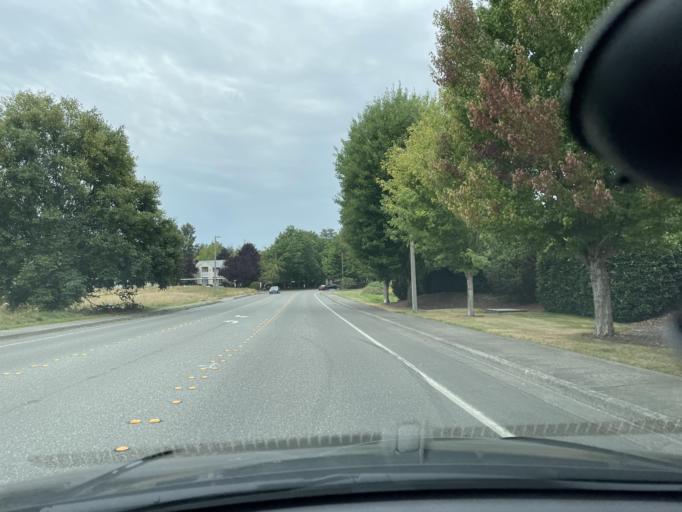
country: US
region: Washington
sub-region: Whatcom County
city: Bellingham
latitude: 48.8050
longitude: -122.4990
